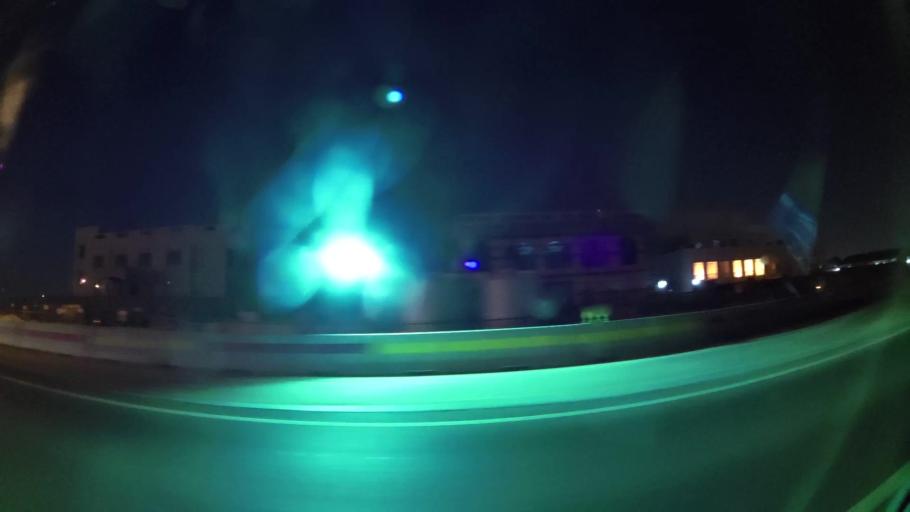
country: QA
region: Baladiyat ar Rayyan
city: Ar Rayyan
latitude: 25.2947
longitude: 51.4442
